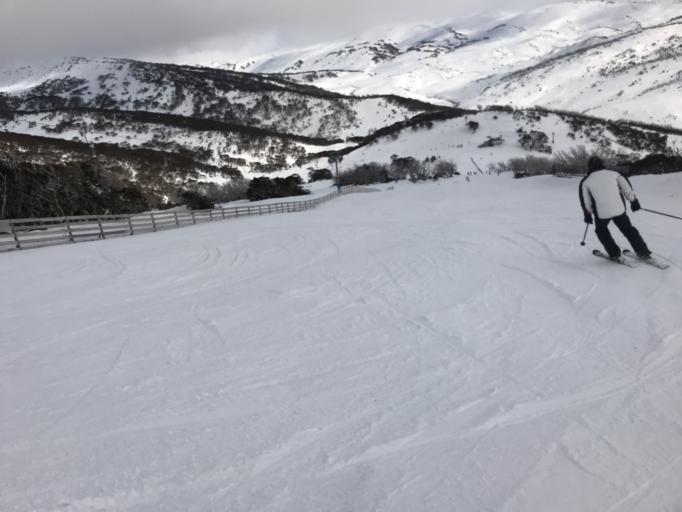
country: AU
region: New South Wales
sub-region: Snowy River
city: Jindabyne
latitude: -36.3809
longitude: 148.3849
